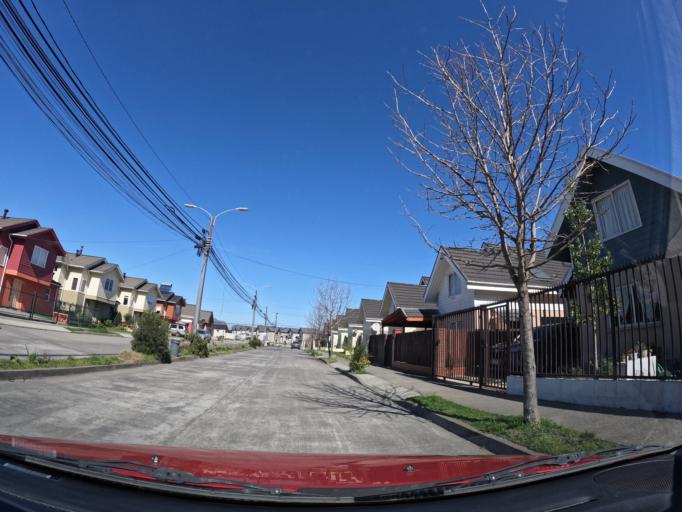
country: CL
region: Biobio
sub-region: Provincia de Concepcion
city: Concepcion
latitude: -36.8893
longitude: -73.1459
